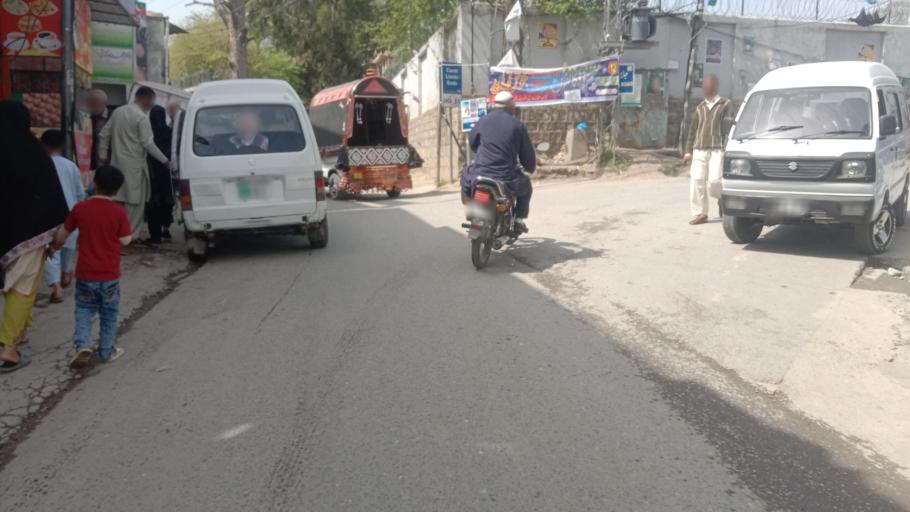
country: PK
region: Khyber Pakhtunkhwa
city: Abbottabad
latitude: 34.1472
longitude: 73.2031
